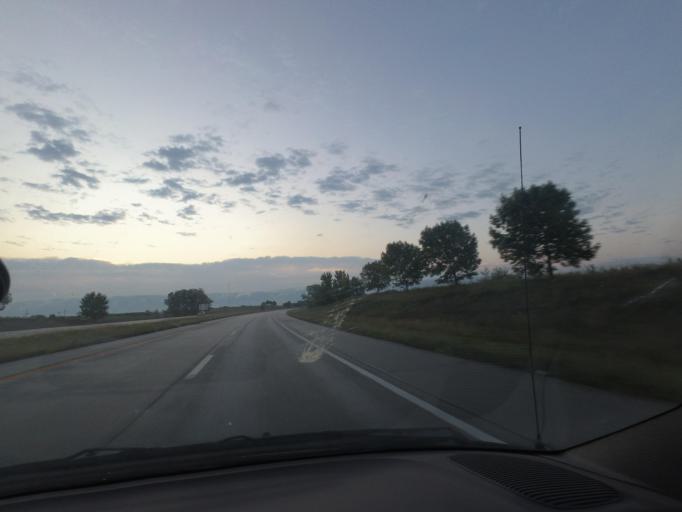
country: US
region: Missouri
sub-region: Macon County
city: Macon
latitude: 39.7598
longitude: -92.5522
